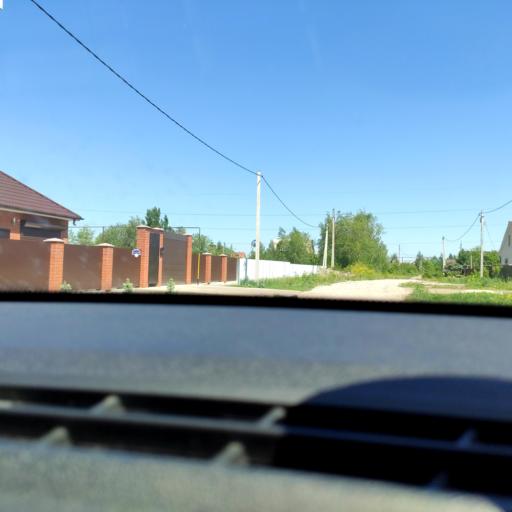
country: RU
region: Samara
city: Tol'yatti
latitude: 53.5593
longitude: 49.3810
